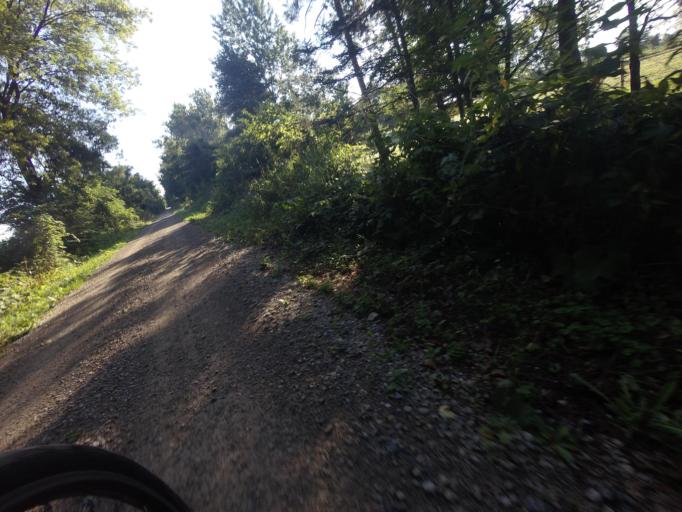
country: CA
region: Ontario
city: Goderich
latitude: 43.7597
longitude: -81.5447
